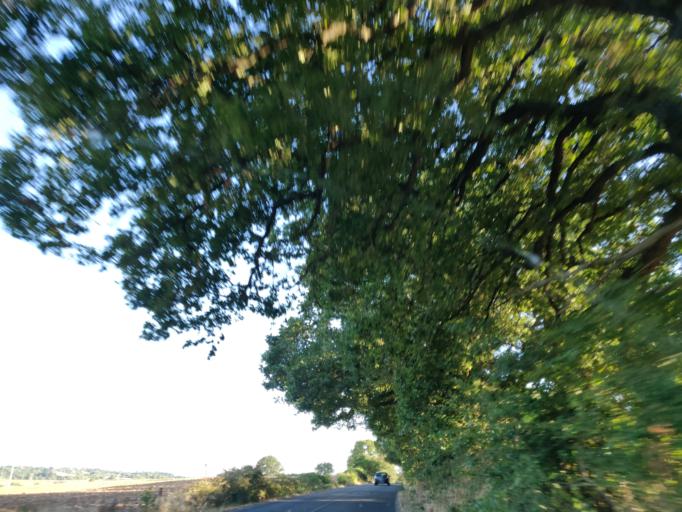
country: IT
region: Latium
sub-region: Provincia di Viterbo
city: Grotte di Castro
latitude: 42.7072
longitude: 11.8799
